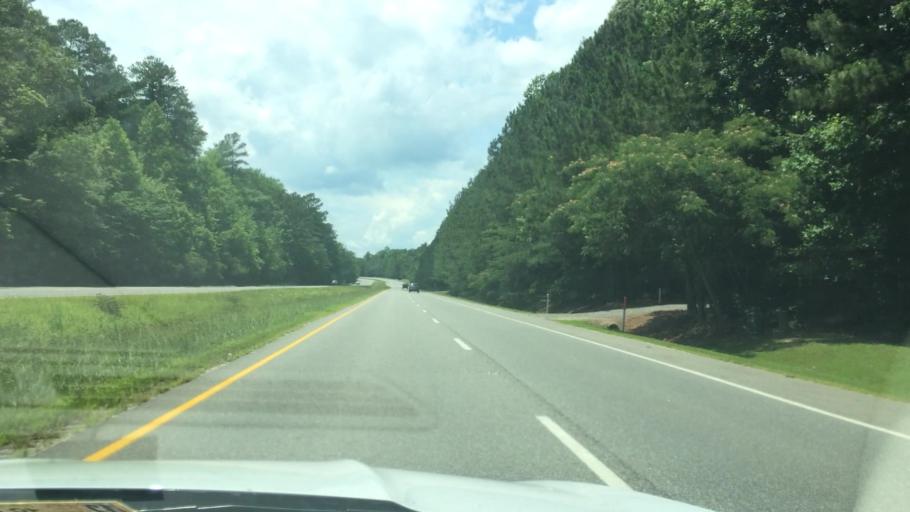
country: US
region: Virginia
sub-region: Middlesex County
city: Saluda
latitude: 37.5643
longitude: -76.6413
